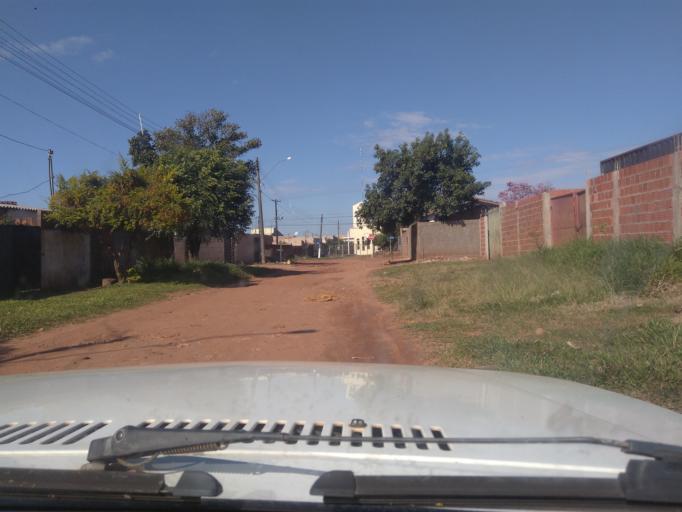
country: BR
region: Mato Grosso do Sul
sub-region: Ponta Pora
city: Ponta Pora
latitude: -22.4998
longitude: -55.7386
